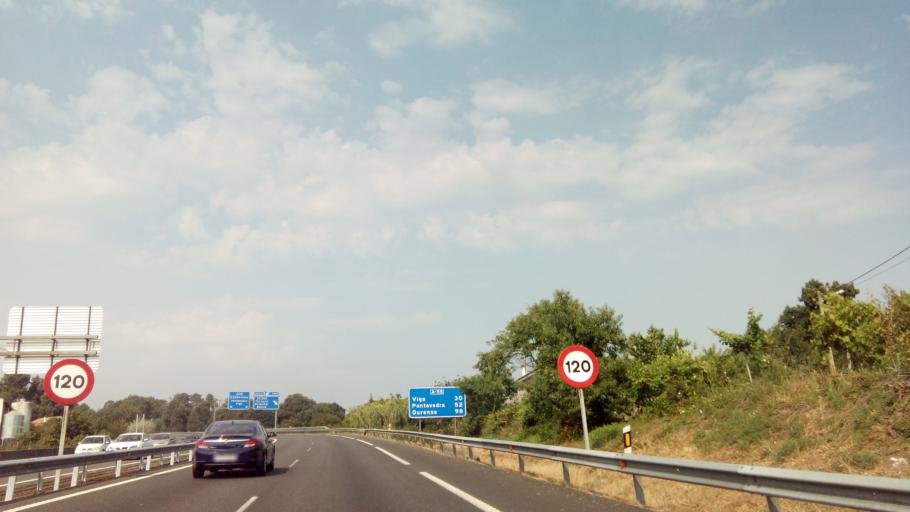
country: ES
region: Galicia
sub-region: Provincia de Pontevedra
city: Tui
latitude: 42.0444
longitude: -8.6583
